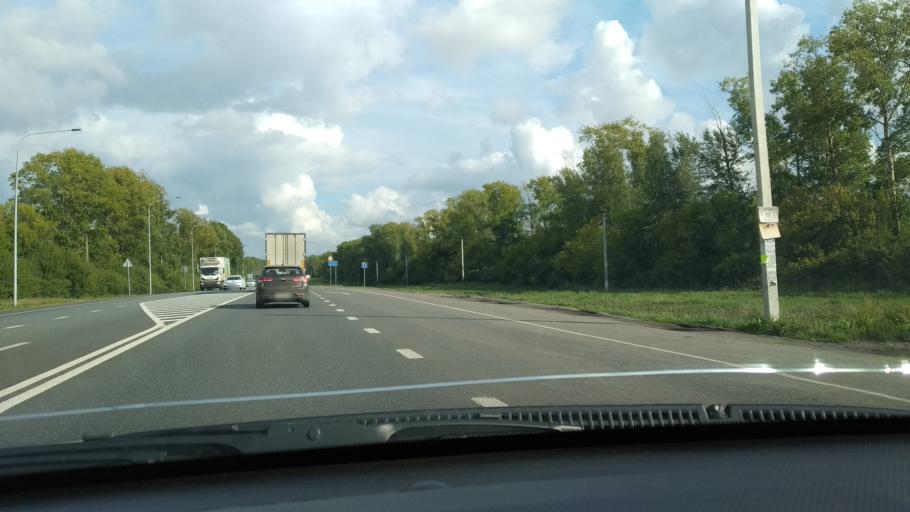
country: RU
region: Tatarstan
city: Stolbishchi
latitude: 55.6554
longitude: 49.3128
